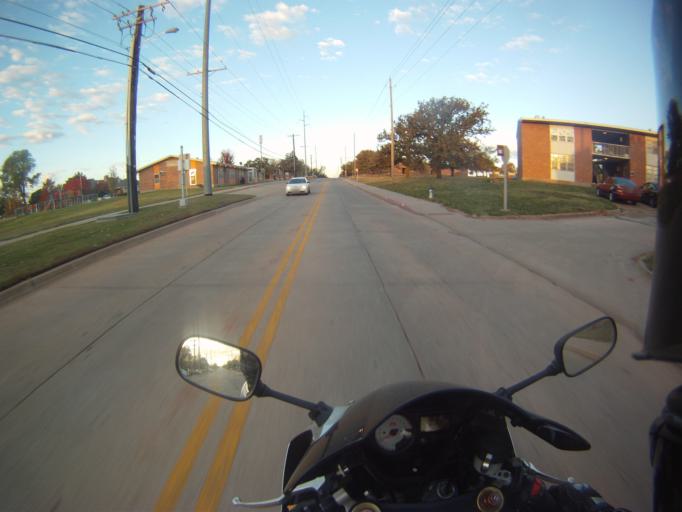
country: US
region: Oklahoma
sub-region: Payne County
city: Stillwater
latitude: 36.1305
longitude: -97.0768
